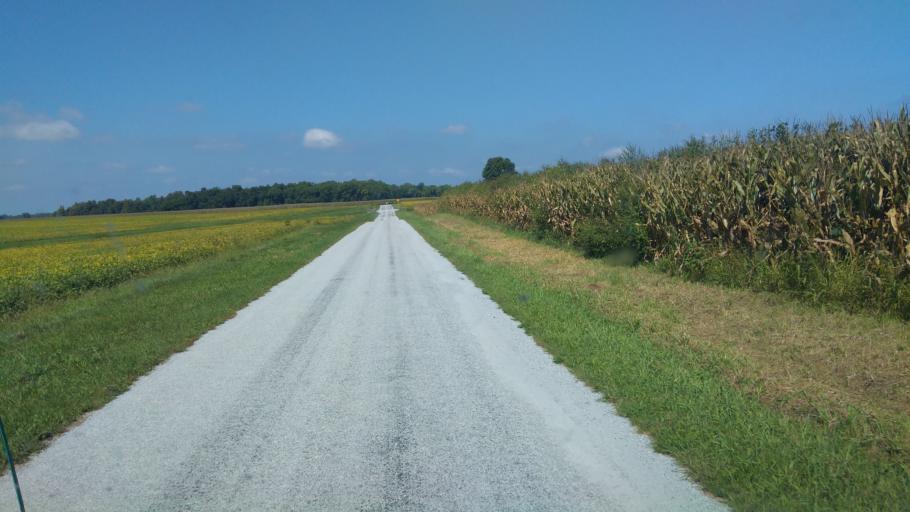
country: US
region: Ohio
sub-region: Hardin County
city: Kenton
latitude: 40.6851
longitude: -83.6093
